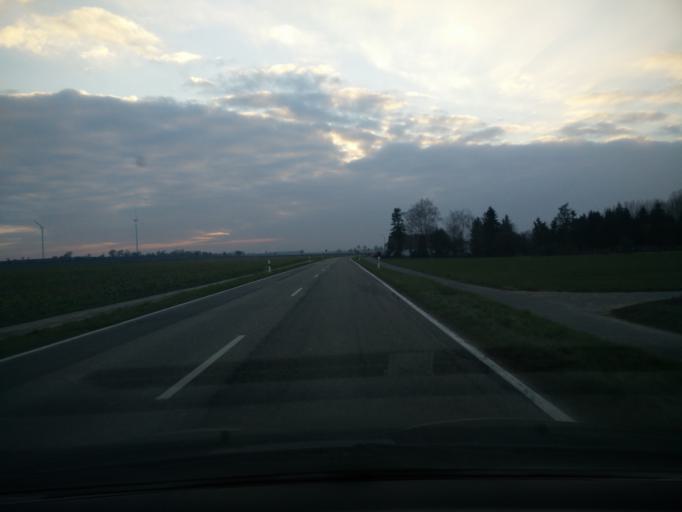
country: DE
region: Rheinland-Pfalz
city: Minfeld
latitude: 49.0932
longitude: 8.1677
